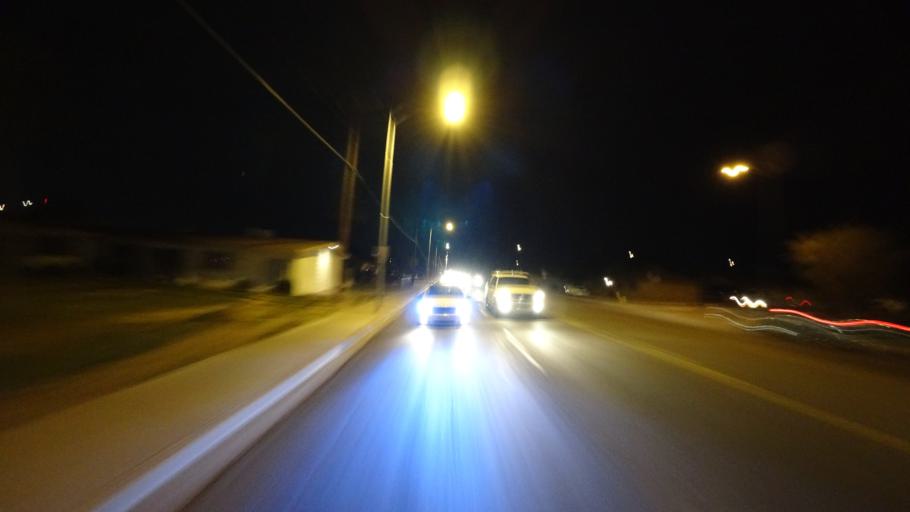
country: US
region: Arizona
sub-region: Maricopa County
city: Mesa
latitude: 33.4012
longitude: -111.8230
